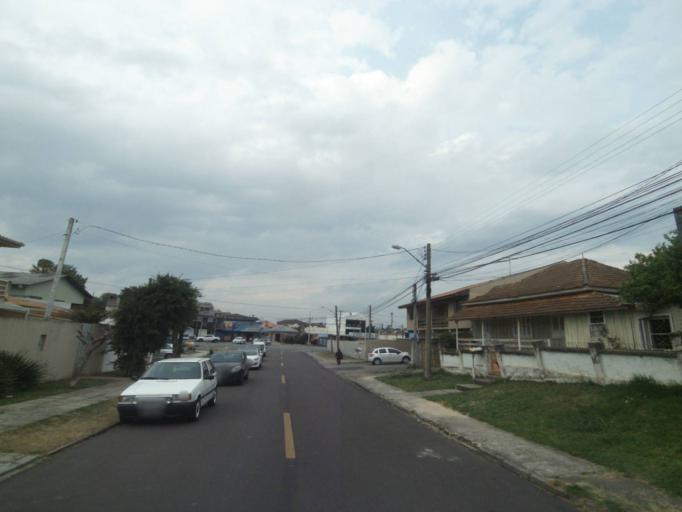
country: BR
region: Parana
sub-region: Pinhais
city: Pinhais
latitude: -25.4750
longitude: -49.2311
